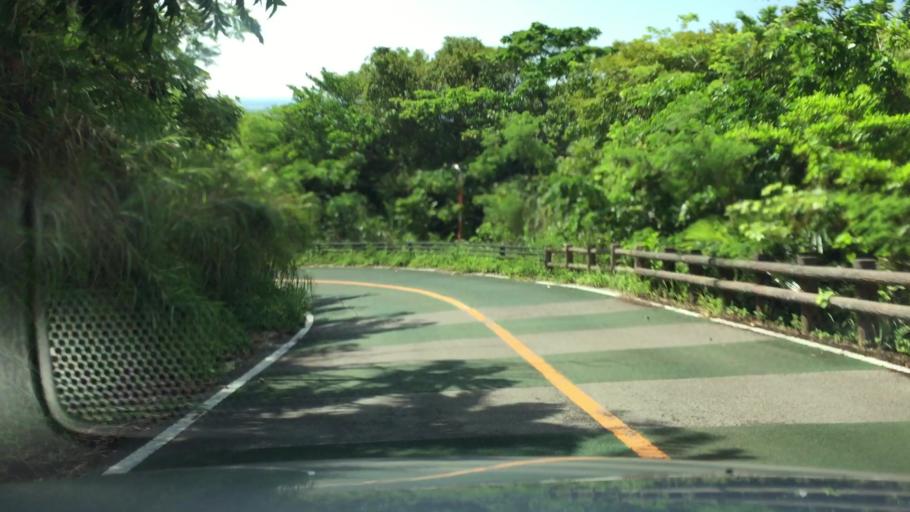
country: JP
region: Okinawa
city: Ishigaki
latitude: 24.3835
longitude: 124.1699
